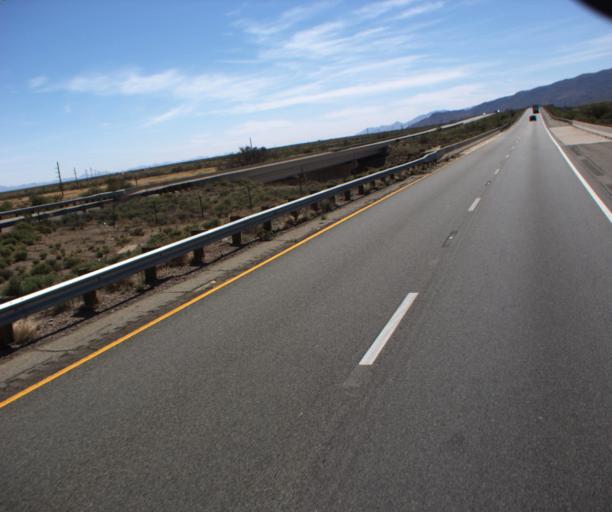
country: US
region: Arizona
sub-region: Cochise County
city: Willcox
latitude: 32.3577
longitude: -109.6132
